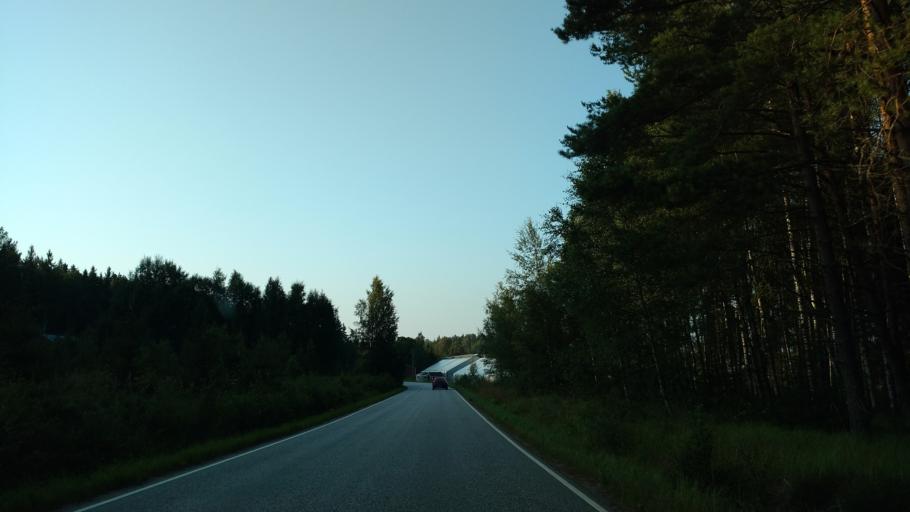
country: FI
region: Varsinais-Suomi
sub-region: Aboland-Turunmaa
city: Dragsfjaerd
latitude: 60.0600
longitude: 22.4514
